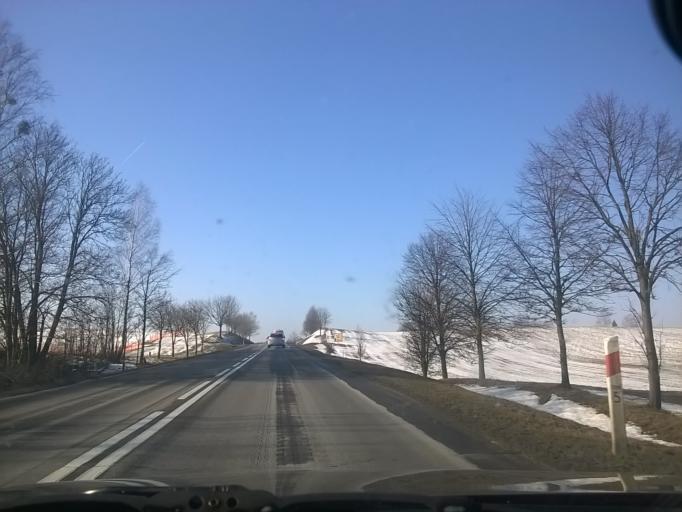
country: PL
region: Warmian-Masurian Voivodeship
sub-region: Powiat mragowski
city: Mragowo
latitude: 53.8406
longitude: 21.1737
